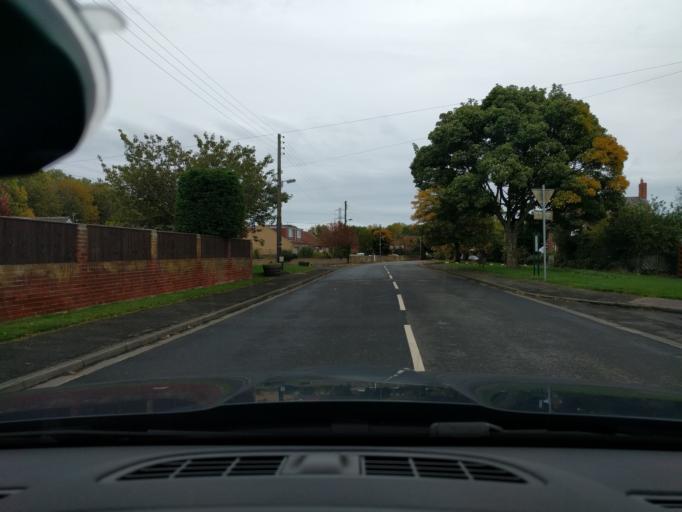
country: GB
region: England
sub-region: Northumberland
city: Ashington
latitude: 55.1447
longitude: -1.5494
